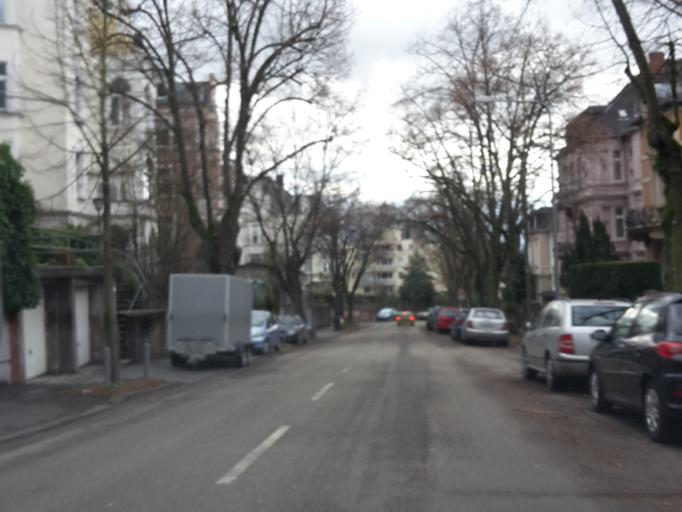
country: DE
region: Hesse
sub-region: Regierungsbezirk Darmstadt
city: Wiesbaden
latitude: 50.0913
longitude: 8.2205
